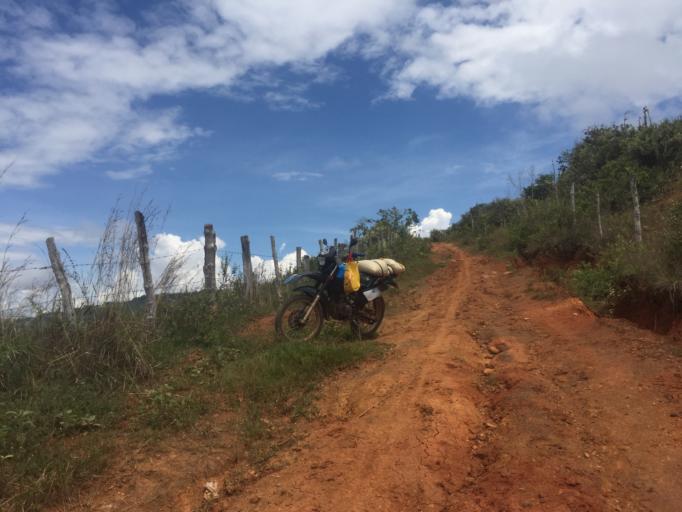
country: CO
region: Valle del Cauca
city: Dagua
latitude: 3.7133
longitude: -76.6032
